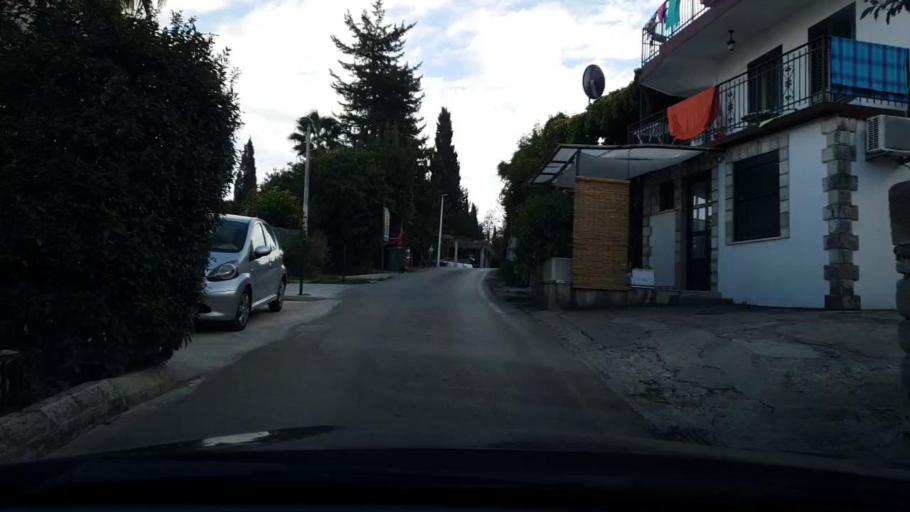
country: ME
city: Igalo
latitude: 42.4369
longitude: 18.5124
